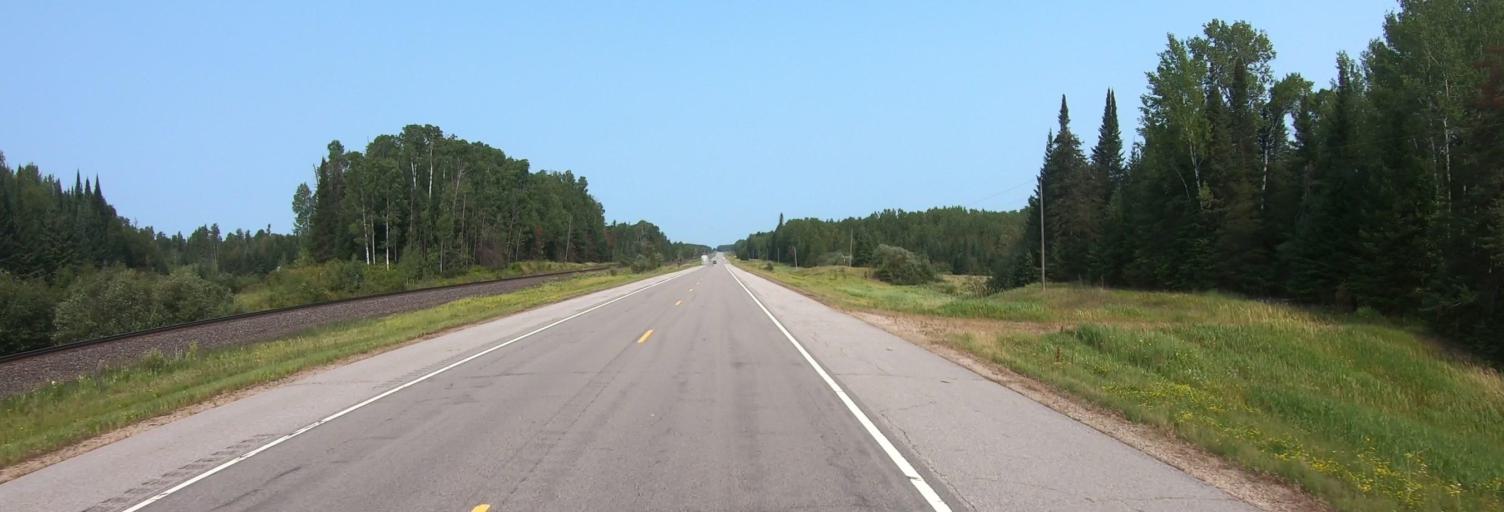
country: US
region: Minnesota
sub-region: Saint Louis County
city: Chisholm
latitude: 48.1555
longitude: -92.8696
